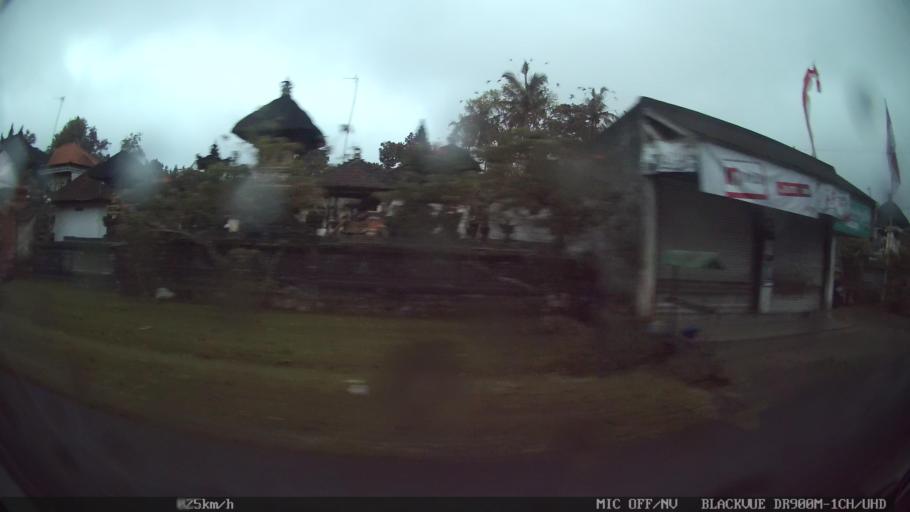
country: ID
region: Bali
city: Banjar Ponggang
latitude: -8.3898
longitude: 115.2604
